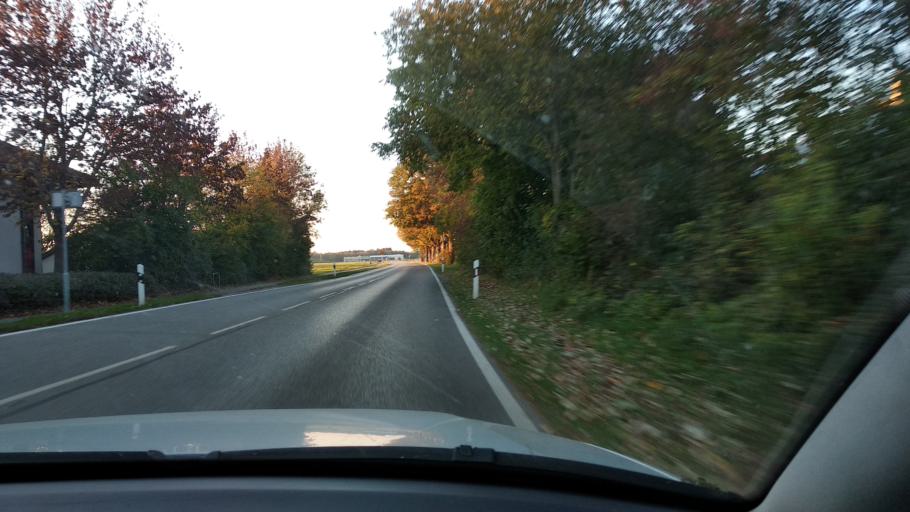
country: DE
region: Bavaria
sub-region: Upper Bavaria
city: Hohenkirchen-Siegertsbrunn
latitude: 48.0240
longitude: 11.7265
